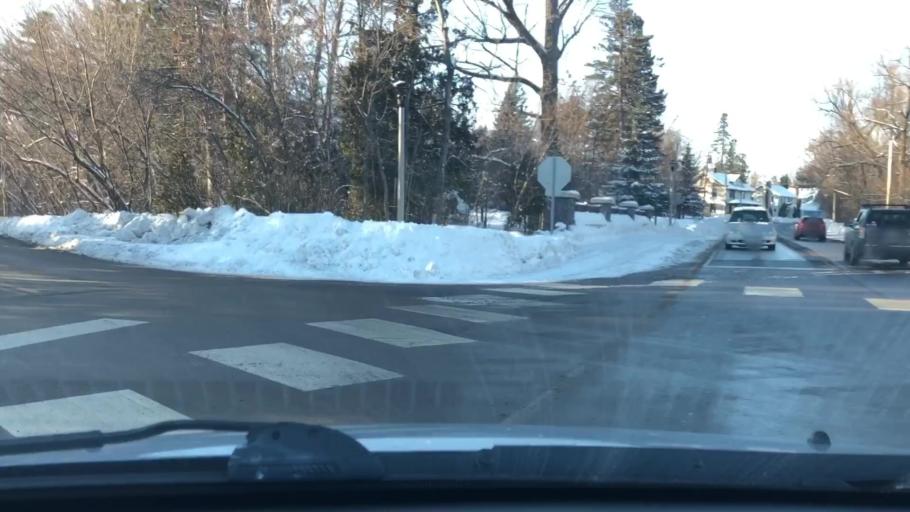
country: US
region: Minnesota
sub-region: Saint Louis County
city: Duluth
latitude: 46.8220
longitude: -92.0697
